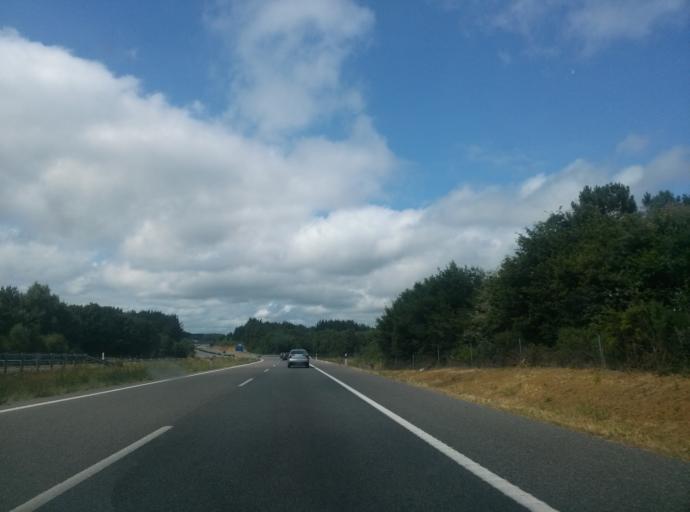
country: ES
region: Galicia
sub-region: Provincia de Lugo
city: Outeiro de Rei
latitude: 43.0695
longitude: -7.5728
